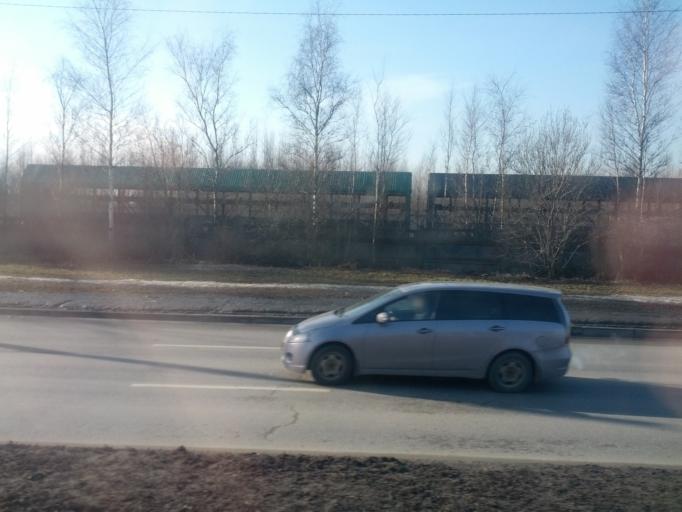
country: RU
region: St.-Petersburg
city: Obukhovo
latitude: 59.9109
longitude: 30.4424
